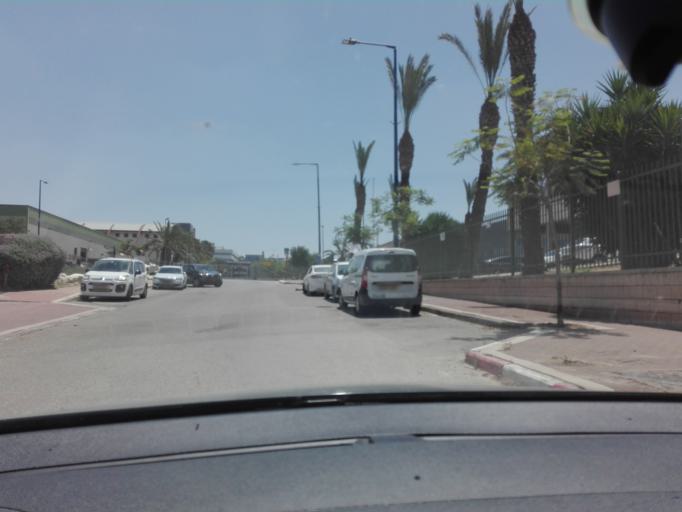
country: IL
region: Southern District
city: Qiryat Gat
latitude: 31.5940
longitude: 34.7829
